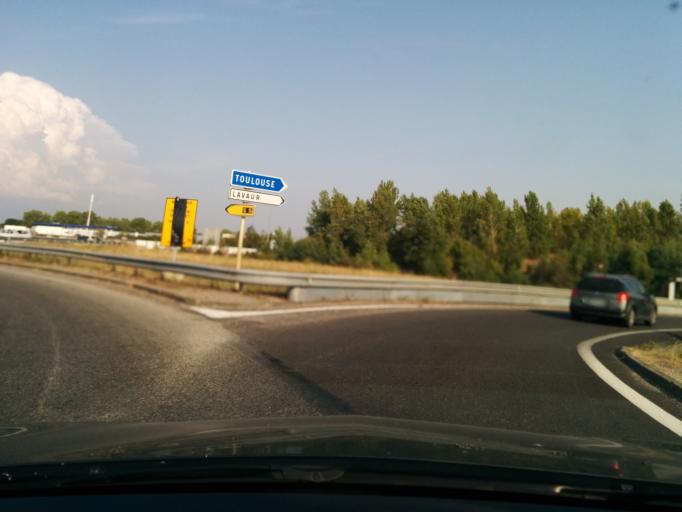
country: FR
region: Midi-Pyrenees
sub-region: Departement du Tarn
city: Brens
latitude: 43.8772
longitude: 1.9049
